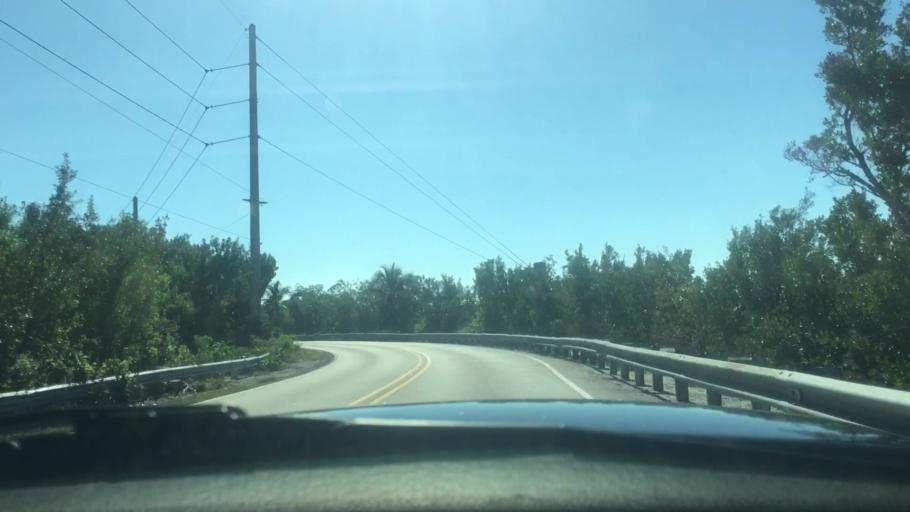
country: US
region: Florida
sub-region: Monroe County
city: North Key Largo
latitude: 25.2973
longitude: -80.3858
